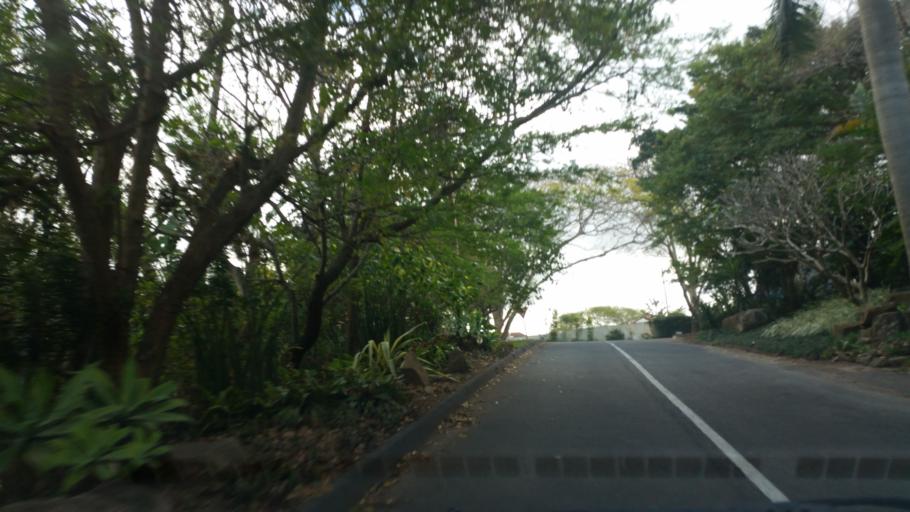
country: ZA
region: KwaZulu-Natal
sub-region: eThekwini Metropolitan Municipality
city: Berea
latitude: -29.8257
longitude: 30.9370
